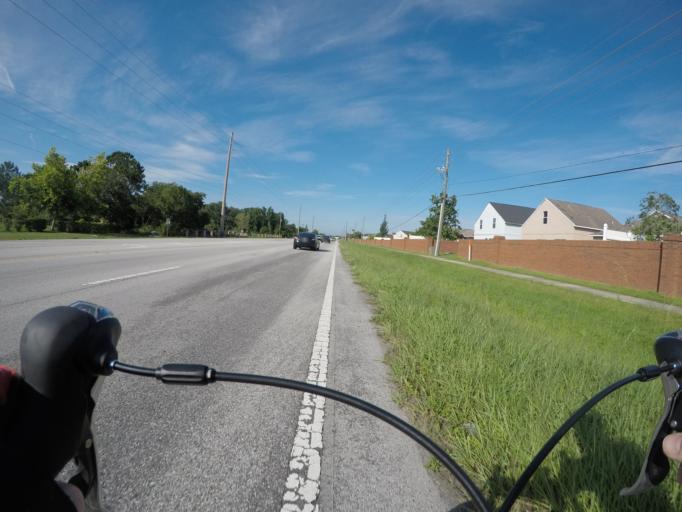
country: US
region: Florida
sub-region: Osceola County
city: Buenaventura Lakes
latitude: 28.3115
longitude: -81.3455
